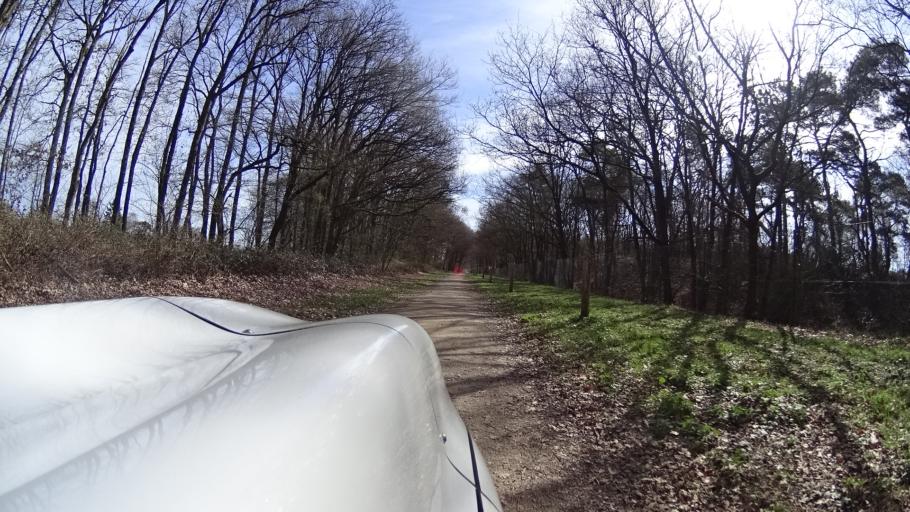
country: NL
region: Limburg
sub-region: Gemeente Gennep
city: Gennep
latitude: 51.6896
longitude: 6.0134
